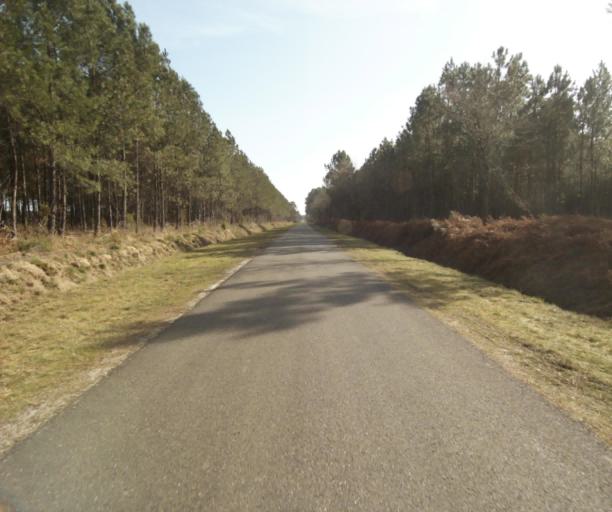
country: FR
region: Aquitaine
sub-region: Departement de la Gironde
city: Grignols
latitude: 44.2269
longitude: -0.1485
